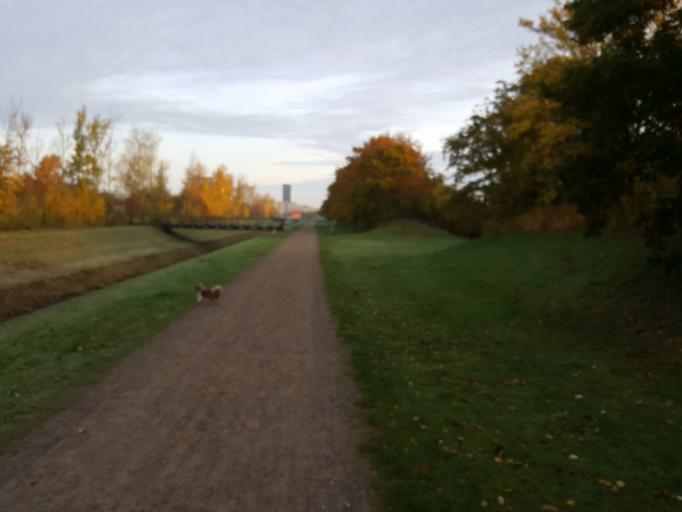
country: DK
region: Capital Region
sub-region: Tarnby Kommune
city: Tarnby
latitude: 55.6135
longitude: 12.5781
